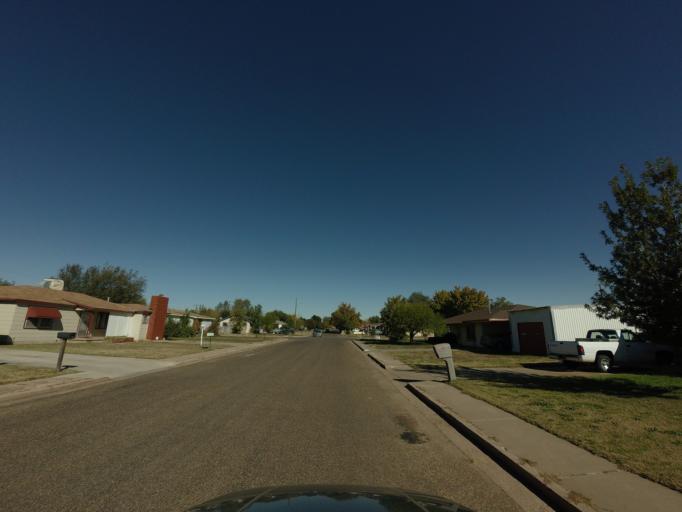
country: US
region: New Mexico
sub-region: Curry County
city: Clovis
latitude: 34.4262
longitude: -103.1990
